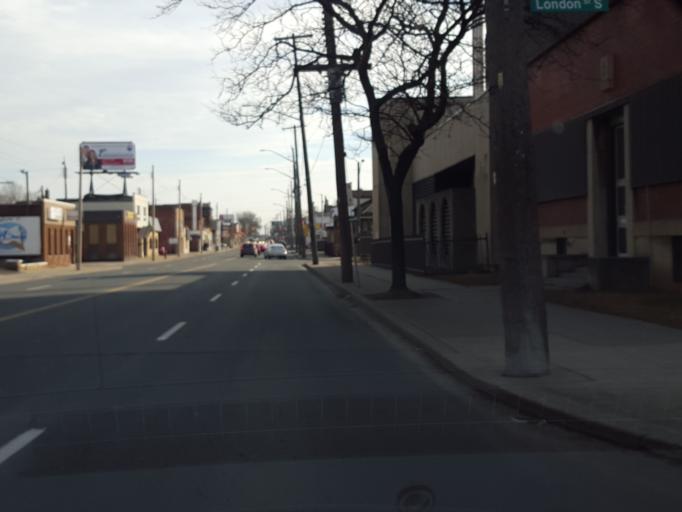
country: CA
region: Ontario
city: Hamilton
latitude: 43.2423
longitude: -79.8187
